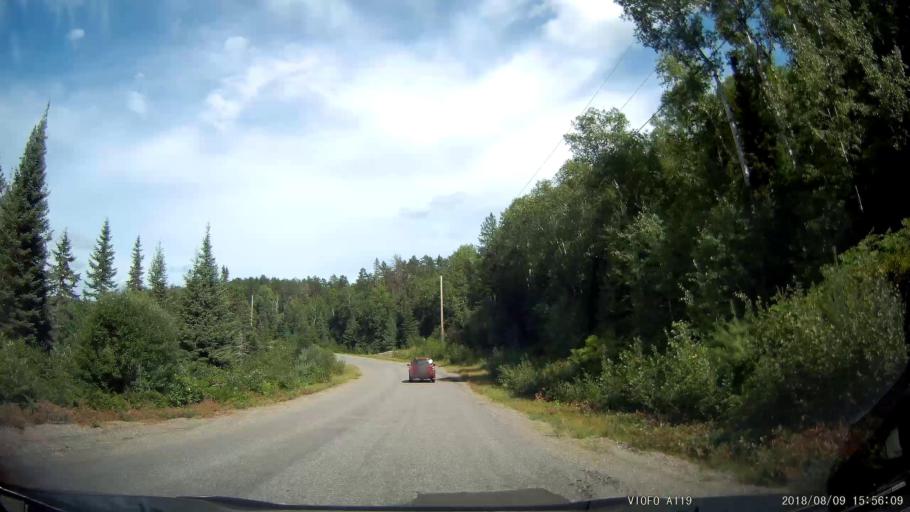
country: CA
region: Ontario
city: Rayside-Balfour
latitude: 46.6053
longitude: -81.5166
